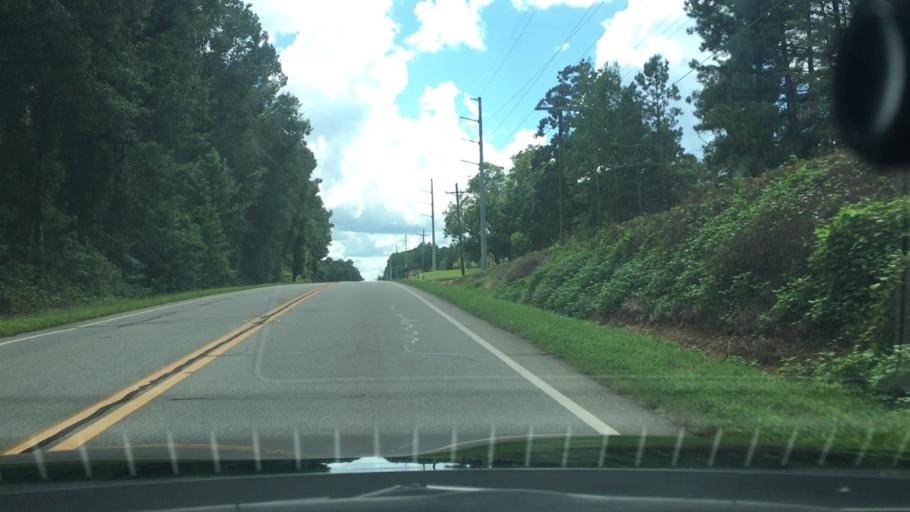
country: US
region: Georgia
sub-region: Putnam County
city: Jefferson
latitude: 33.3737
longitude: -83.3259
